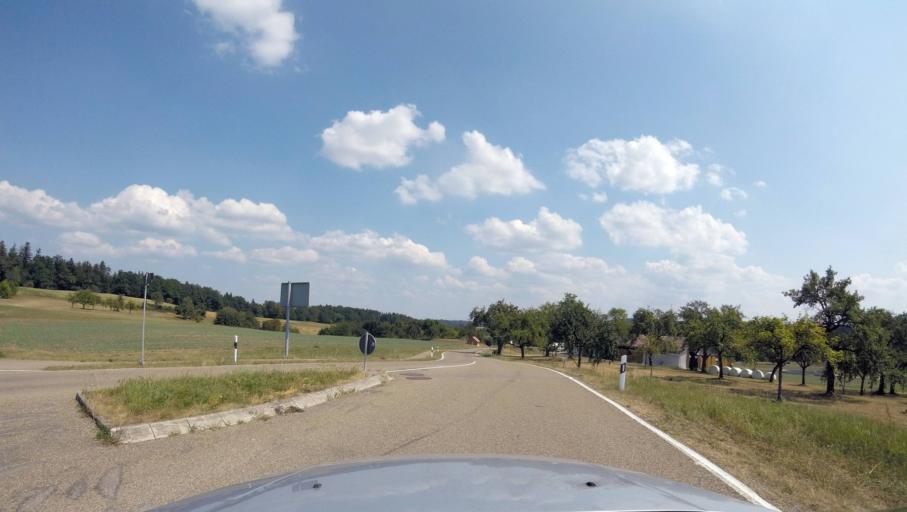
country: DE
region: Baden-Wuerttemberg
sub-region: Regierungsbezirk Stuttgart
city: Althutte
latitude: 48.9486
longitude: 9.5661
